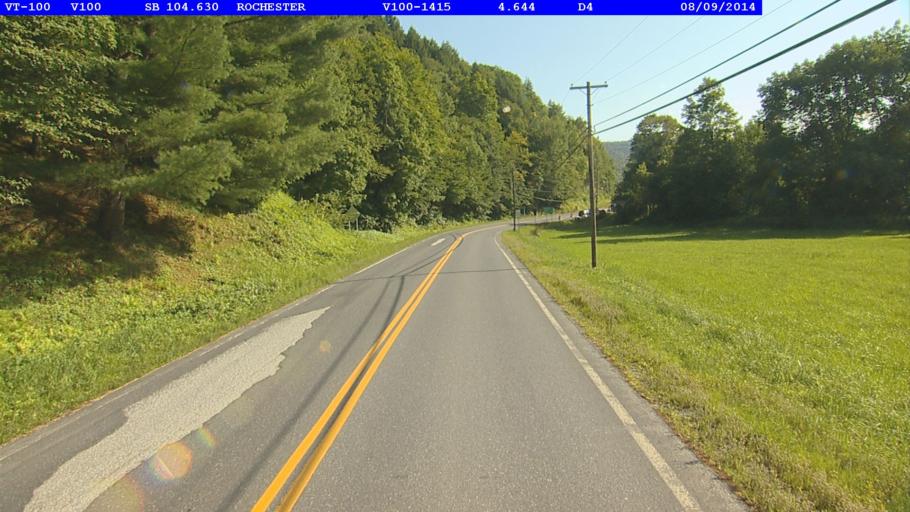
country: US
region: Vermont
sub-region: Orange County
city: Randolph
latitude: 43.8653
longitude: -72.8089
